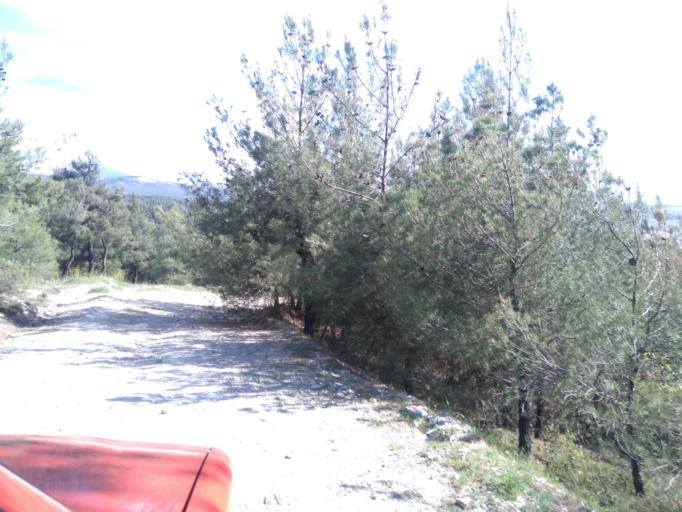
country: GR
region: Central Macedonia
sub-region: Nomos Thessalonikis
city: Triandria
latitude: 40.6342
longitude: 22.9800
